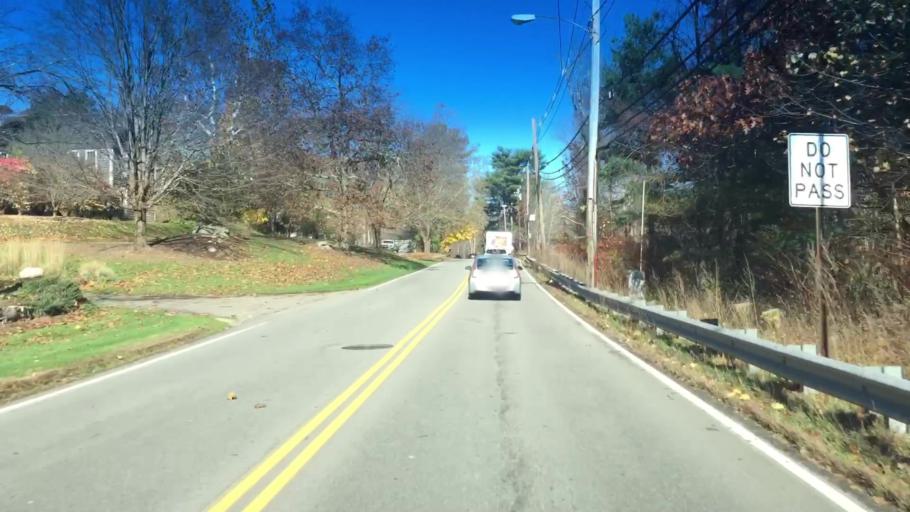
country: US
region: Massachusetts
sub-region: Norfolk County
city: Medfield
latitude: 42.1754
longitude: -71.2995
